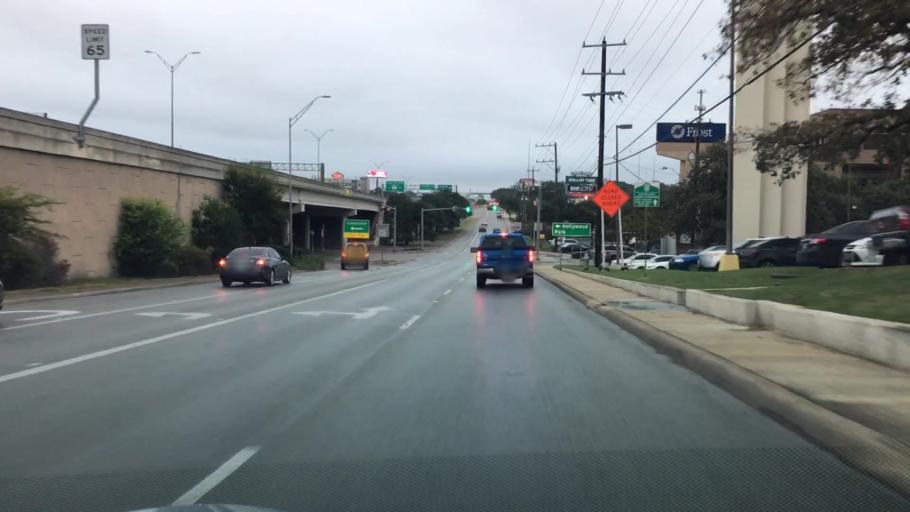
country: US
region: Texas
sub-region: Bexar County
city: Hollywood Park
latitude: 29.5918
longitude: -98.4731
